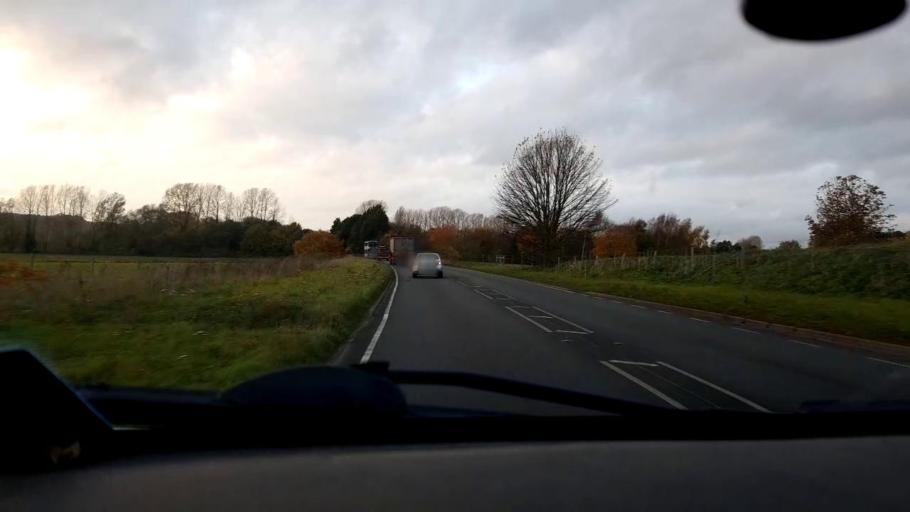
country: GB
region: England
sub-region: Norfolk
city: Costessey
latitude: 52.7047
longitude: 1.1543
